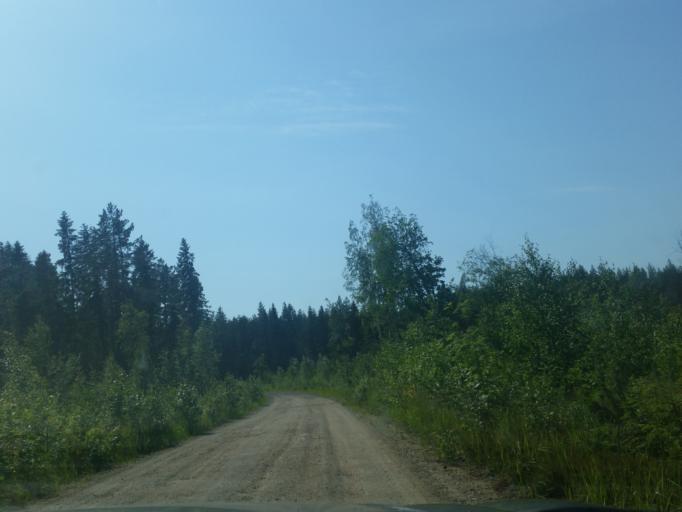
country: FI
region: Northern Savo
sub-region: Sisae-Savo
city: Tervo
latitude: 63.0915
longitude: 26.5888
